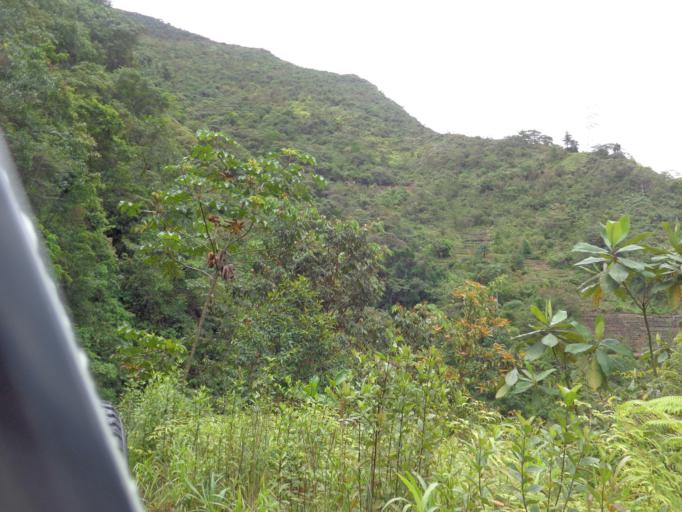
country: BO
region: La Paz
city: Coroico
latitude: -16.0502
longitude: -68.0085
